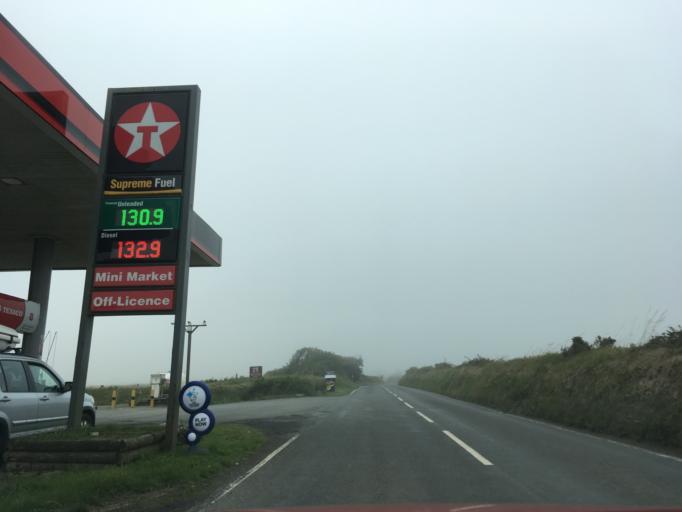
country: GB
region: Wales
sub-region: Pembrokeshire
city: Saint David's
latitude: 51.8807
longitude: -5.2502
